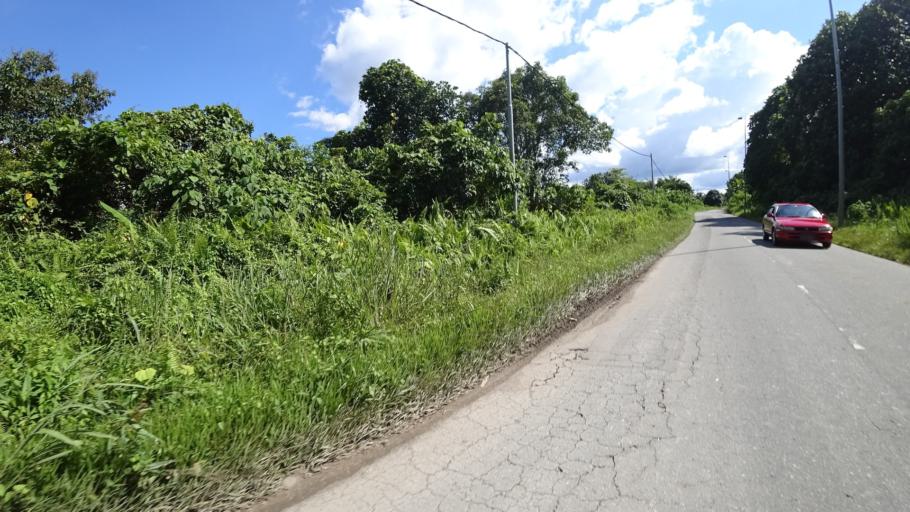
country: BN
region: Tutong
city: Tutong
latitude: 4.7662
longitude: 114.7959
